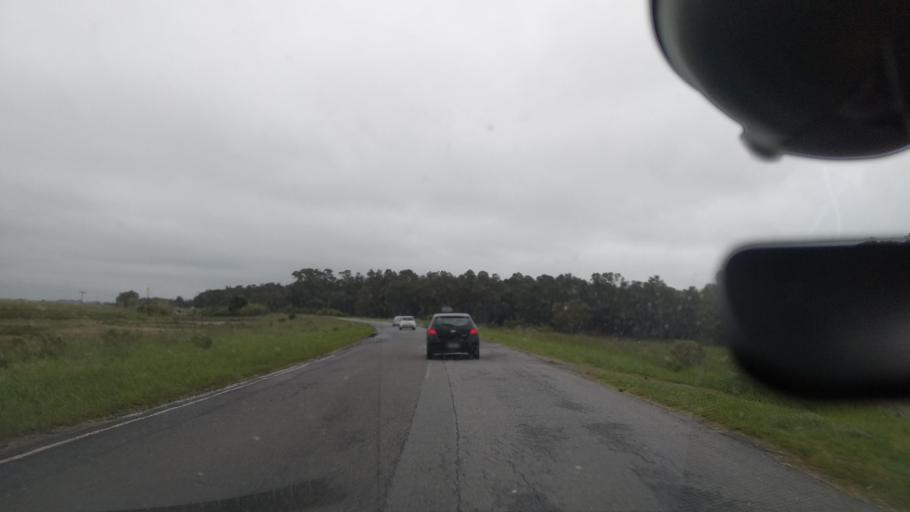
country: AR
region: Buenos Aires
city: Veronica
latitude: -35.4687
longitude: -57.3239
